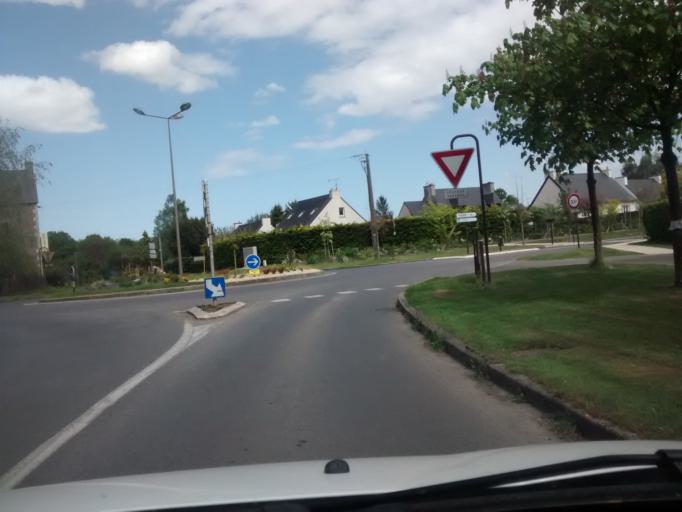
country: FR
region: Brittany
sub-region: Departement des Cotes-d'Armor
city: Taden
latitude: 48.4747
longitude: -2.0246
